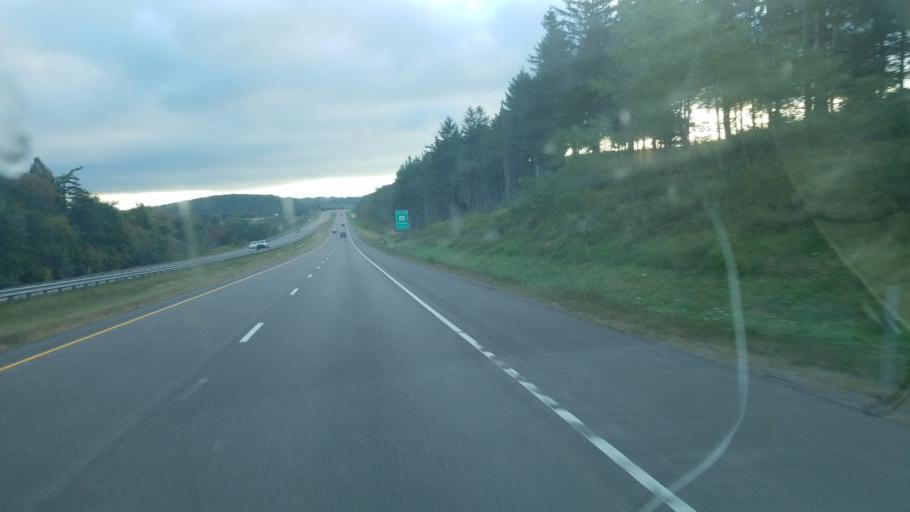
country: US
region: Maryland
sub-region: Allegany County
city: Frostburg
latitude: 39.6847
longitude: -78.9923
